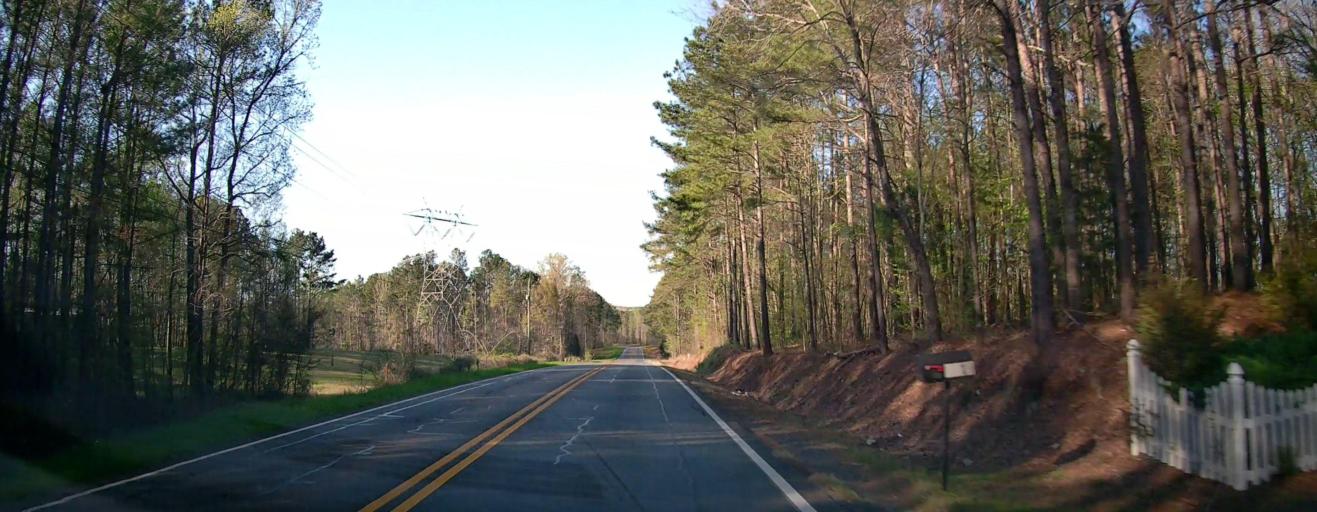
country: US
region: Georgia
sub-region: Monroe County
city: Forsyth
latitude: 33.1143
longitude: -83.9444
